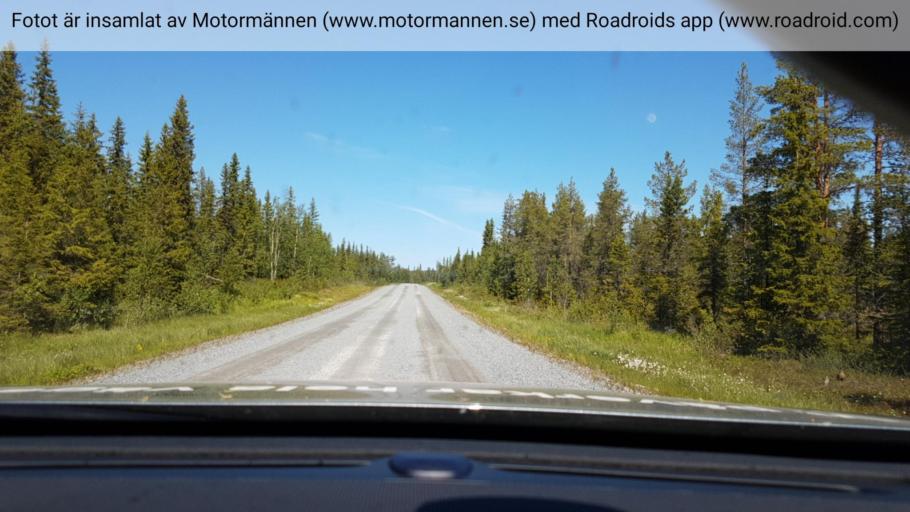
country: SE
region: Vaesterbotten
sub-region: Vilhelmina Kommun
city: Sjoberg
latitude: 64.6947
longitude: 15.7573
